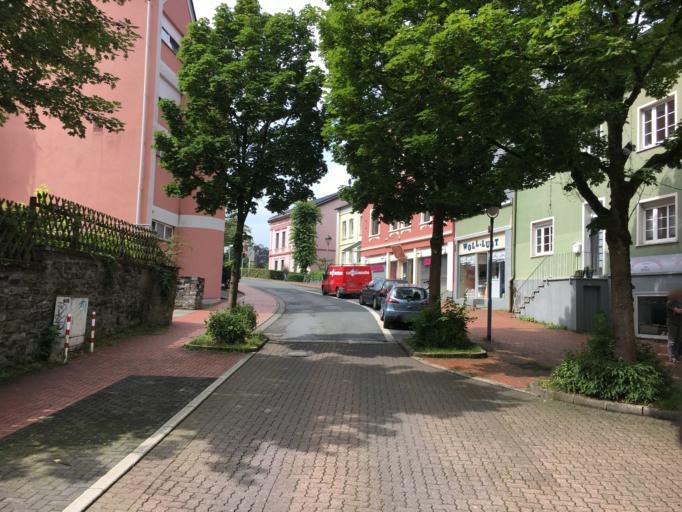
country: DE
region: North Rhine-Westphalia
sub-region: Regierungsbezirk Arnsberg
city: Luedenscheid
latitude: 51.2190
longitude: 7.6380
